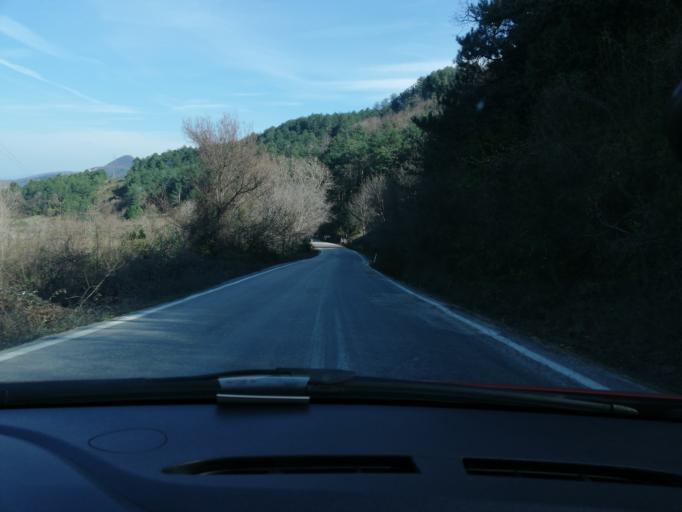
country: TR
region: Bartin
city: Kurucasile
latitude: 41.8334
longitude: 32.6968
